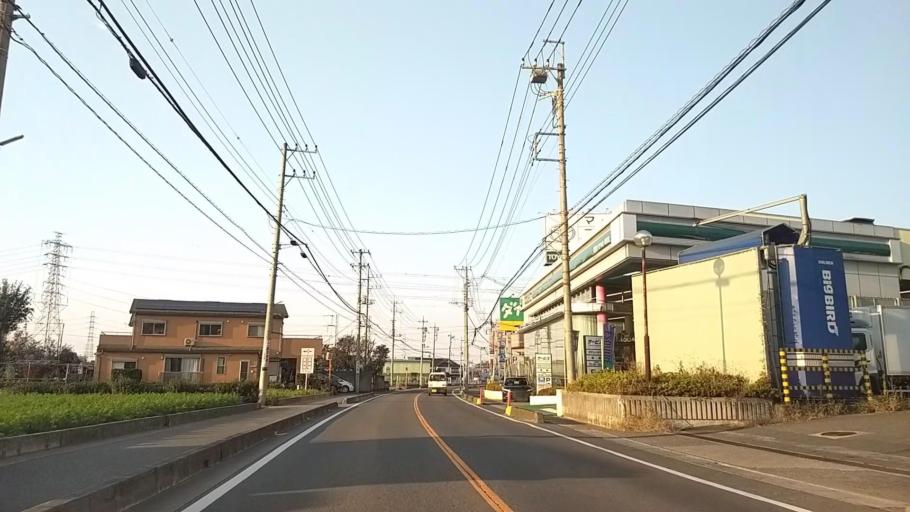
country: JP
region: Saitama
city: Tokorozawa
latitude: 35.8316
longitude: 139.4649
